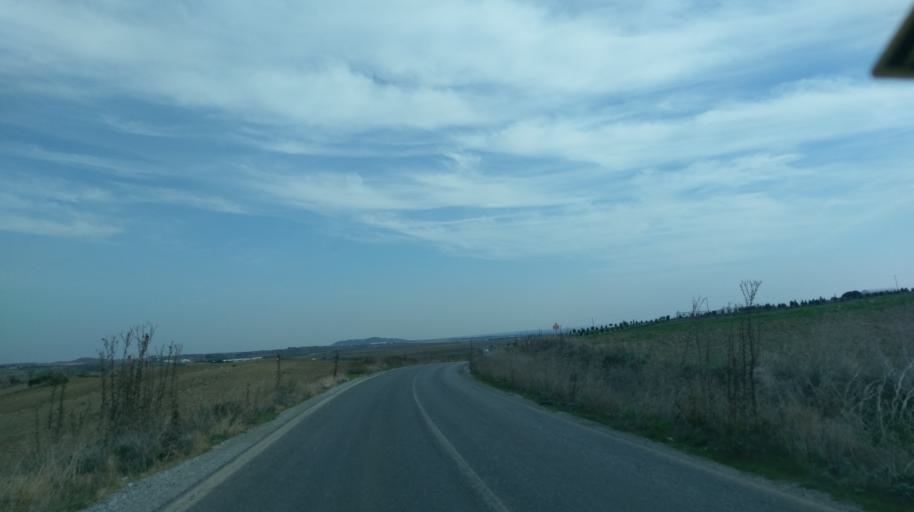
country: CY
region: Keryneia
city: Lapithos
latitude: 35.2551
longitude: 33.1413
